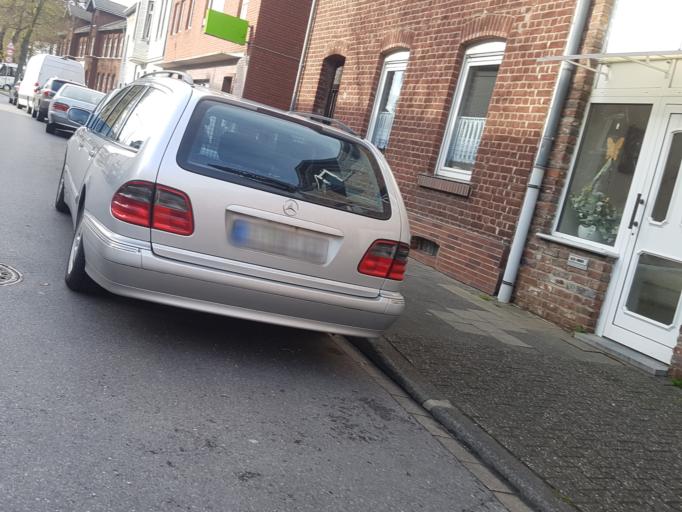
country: DE
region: North Rhine-Westphalia
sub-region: Regierungsbezirk Koln
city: Wurselen
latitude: 50.7806
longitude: 6.1622
